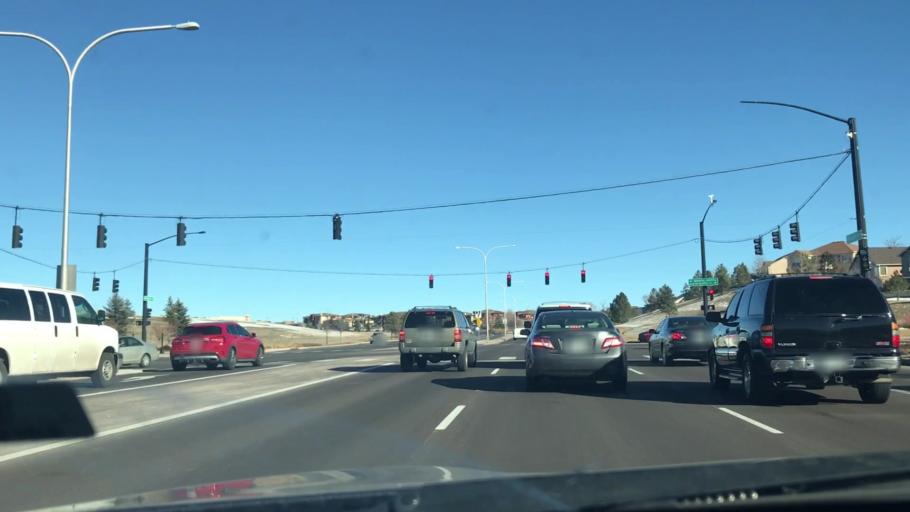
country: US
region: Colorado
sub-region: El Paso County
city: Black Forest
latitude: 38.9658
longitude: -104.7517
